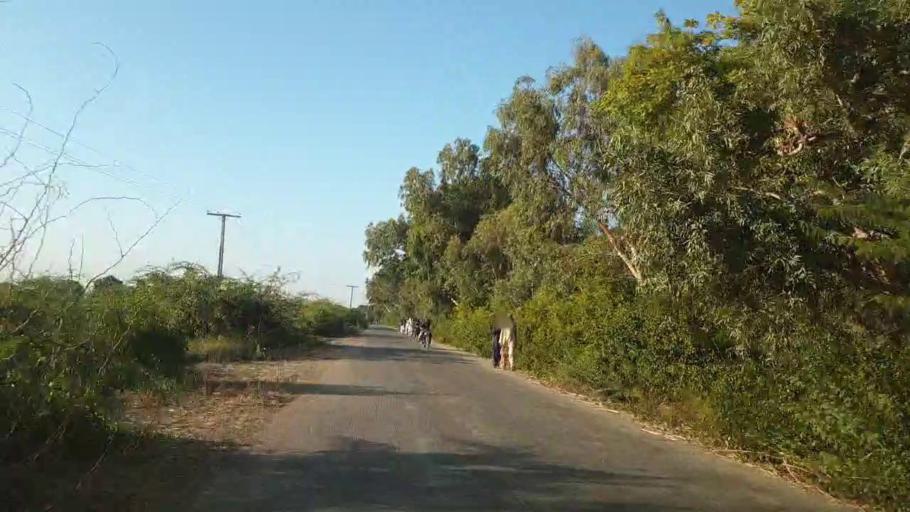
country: PK
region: Sindh
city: Mirpur Khas
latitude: 25.6541
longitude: 69.0974
